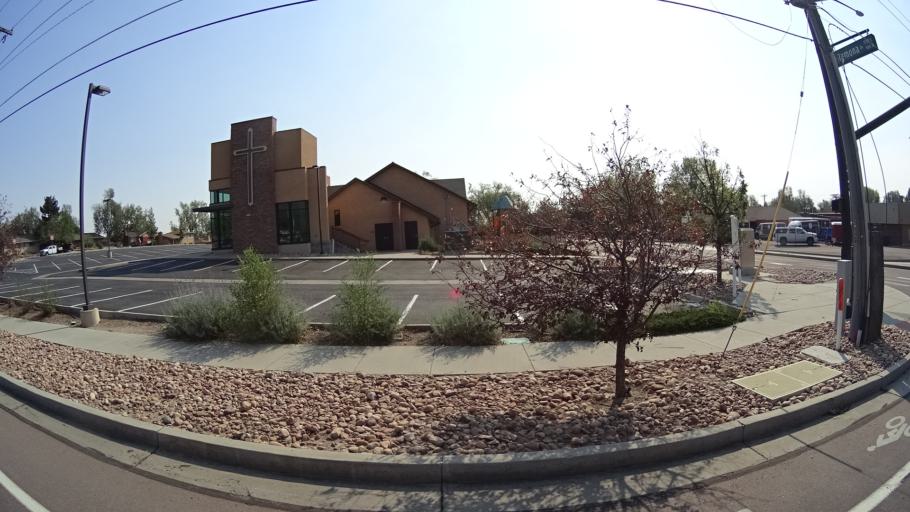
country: US
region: Colorado
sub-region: El Paso County
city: Colorado Springs
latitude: 38.8092
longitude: -104.8407
